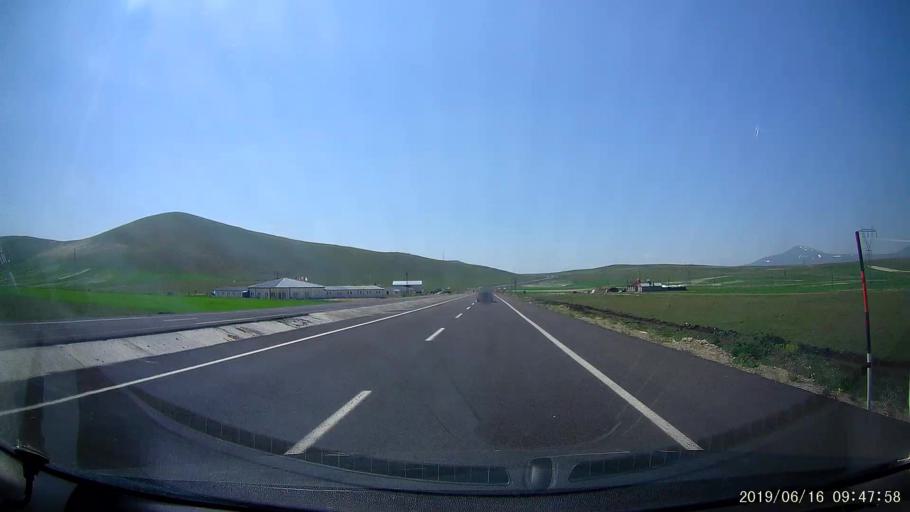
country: TR
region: Kars
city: Digor
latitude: 40.4387
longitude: 43.3497
